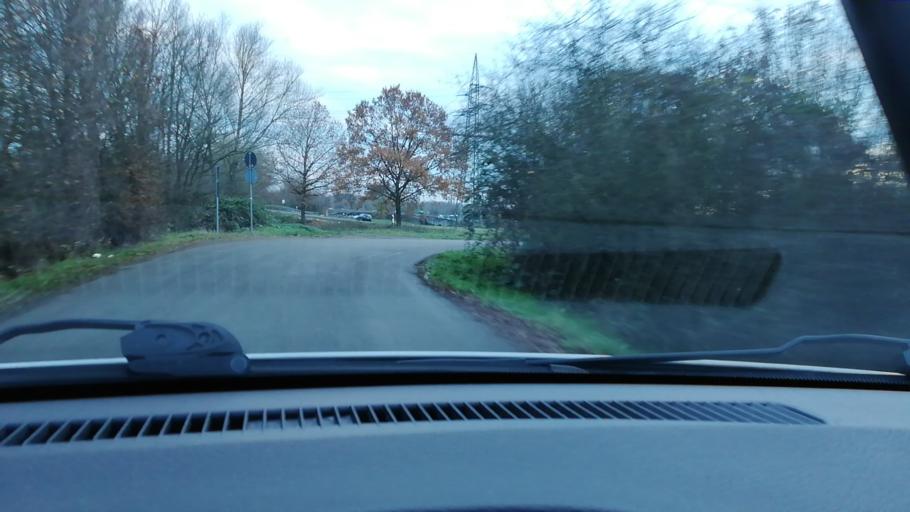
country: DE
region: Hesse
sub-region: Regierungsbezirk Darmstadt
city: Erlensee
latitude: 50.1527
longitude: 8.9979
